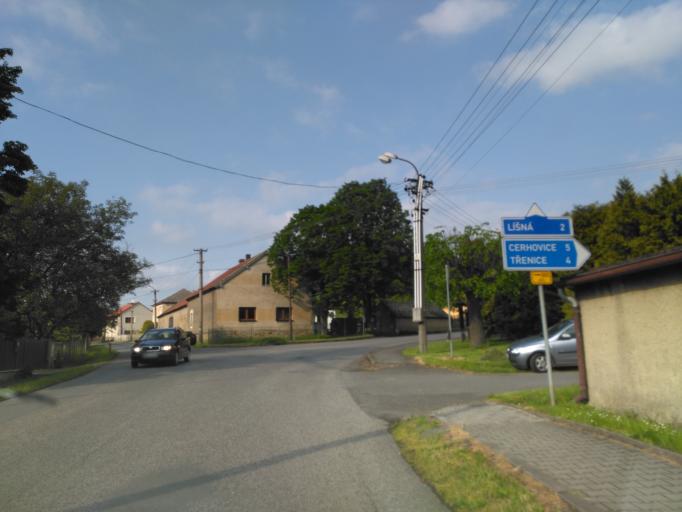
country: CZ
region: Plzensky
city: Zbiroh
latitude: 49.8699
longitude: 13.7952
